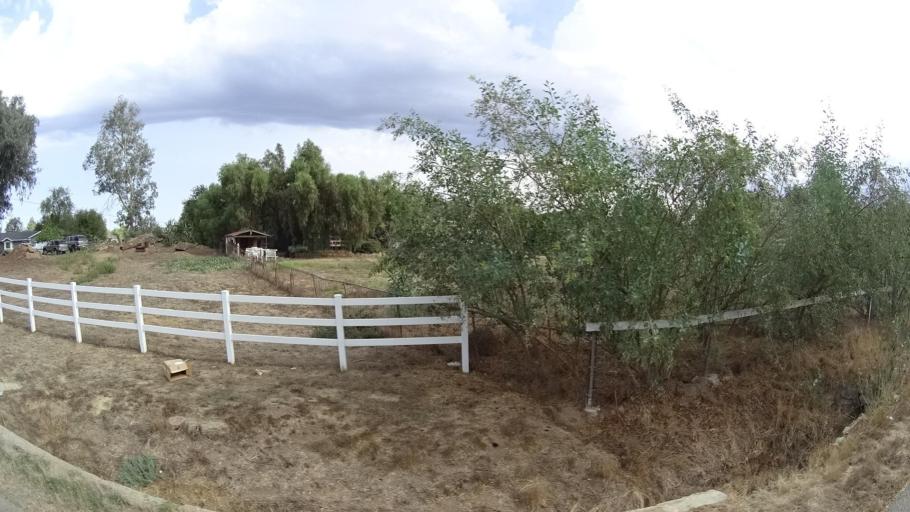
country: US
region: California
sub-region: San Diego County
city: Ramona
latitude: 33.0227
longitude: -116.9266
